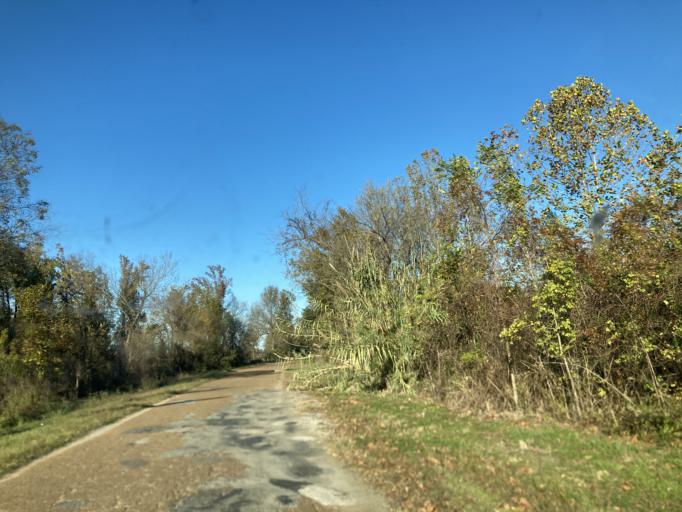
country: US
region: Mississippi
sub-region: Yazoo County
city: Yazoo City
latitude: 32.8138
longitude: -90.4506
